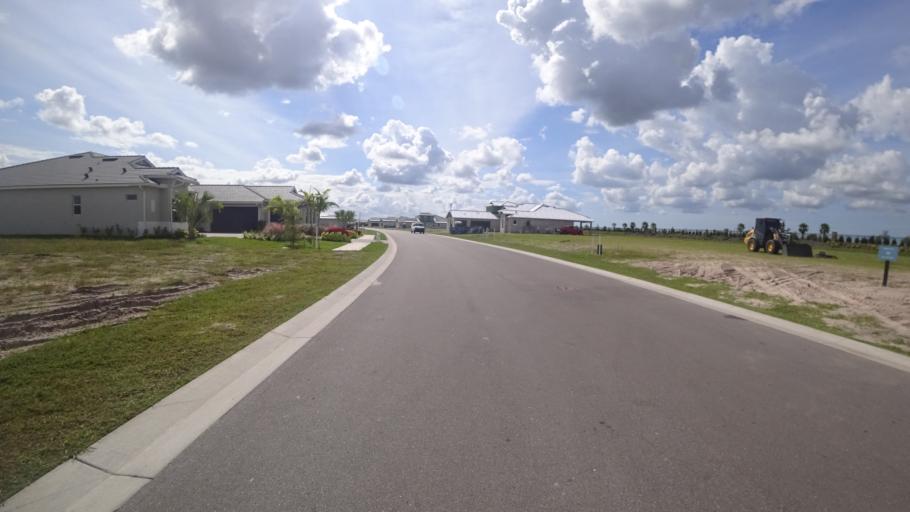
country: US
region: Florida
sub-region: Sarasota County
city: The Meadows
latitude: 27.3943
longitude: -82.3610
